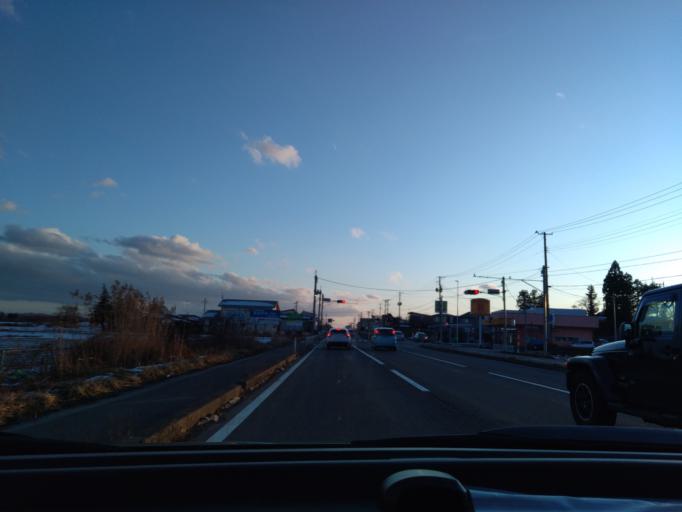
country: JP
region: Iwate
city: Hanamaki
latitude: 39.4452
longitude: 141.1364
